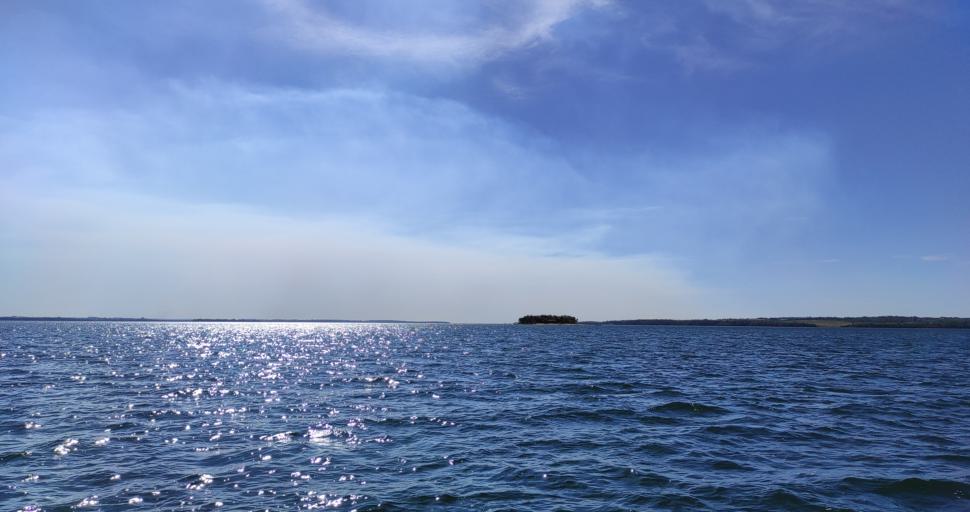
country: PY
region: Itapua
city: San Juan del Parana
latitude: -27.3438
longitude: -55.9412
